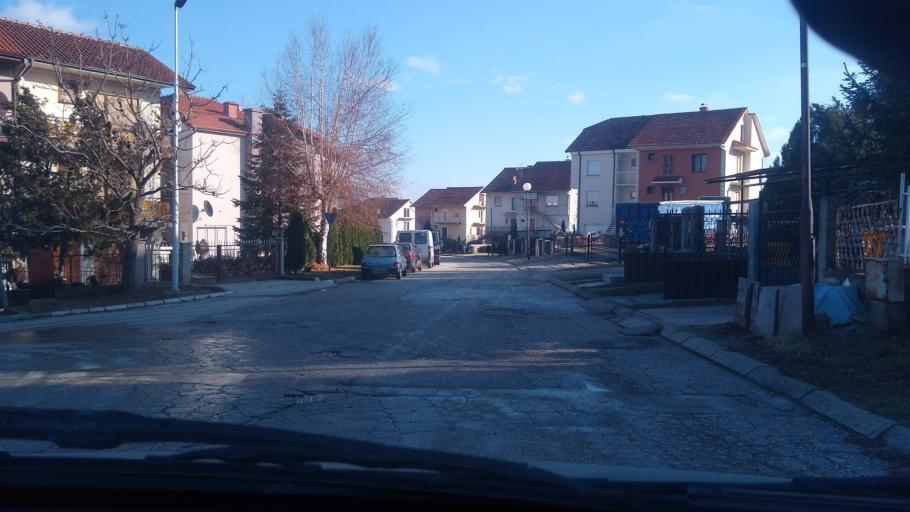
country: MK
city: Bistrica
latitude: 41.0036
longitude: 21.3457
